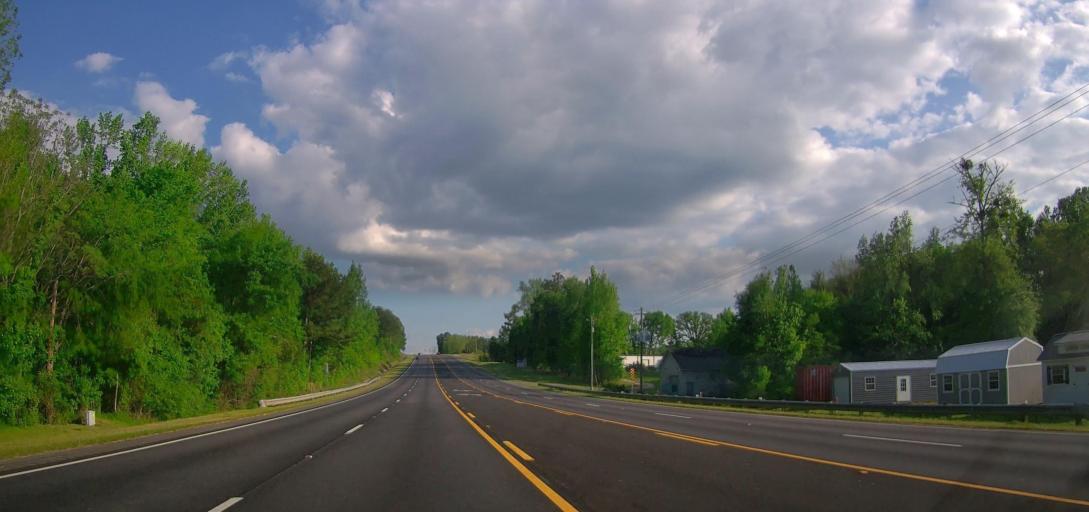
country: US
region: Georgia
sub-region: Baldwin County
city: Milledgeville
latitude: 33.1616
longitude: -83.2783
